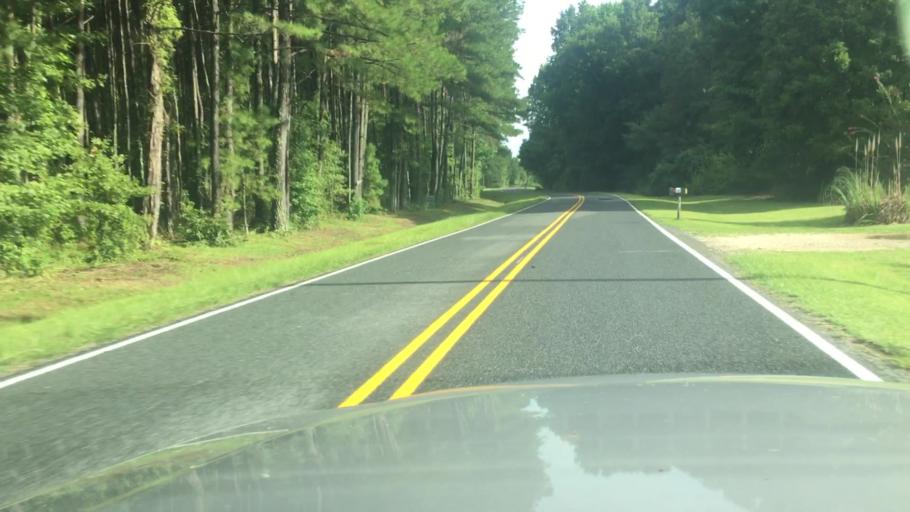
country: US
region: North Carolina
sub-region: Cumberland County
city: Eastover
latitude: 35.1605
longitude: -78.8539
